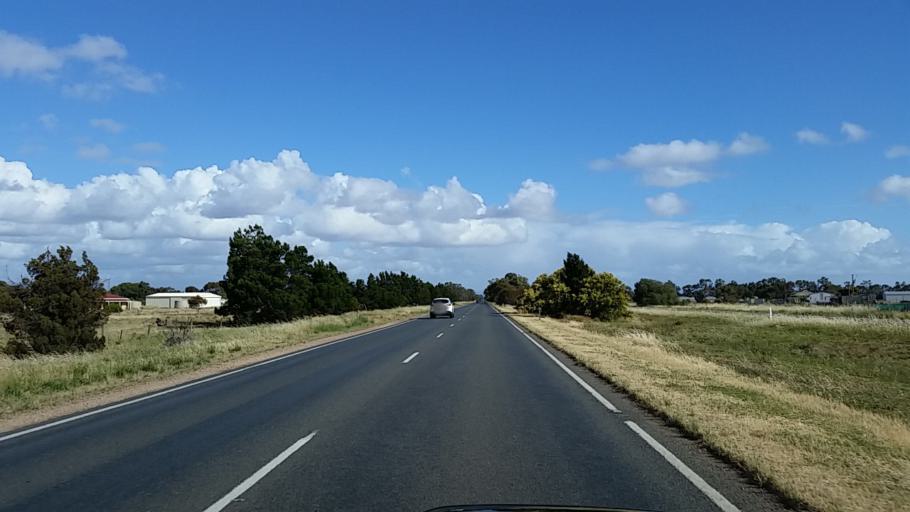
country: AU
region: South Australia
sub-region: Mallala
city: Two Wells
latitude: -34.6160
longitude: 138.5190
